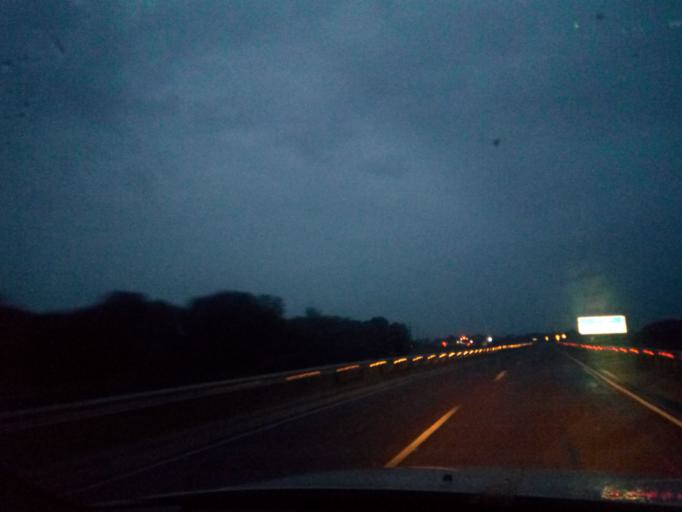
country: RU
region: Primorskiy
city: Dal'nerechensk
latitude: 45.9133
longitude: 133.7672
